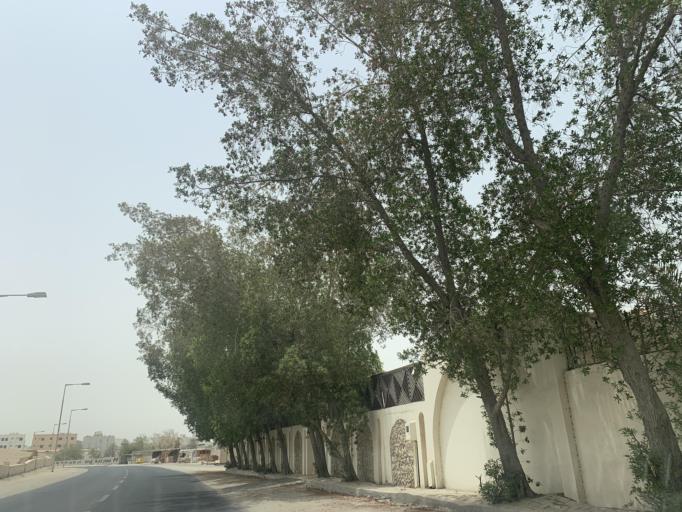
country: BH
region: Manama
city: Jidd Hafs
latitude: 26.2142
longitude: 50.5000
